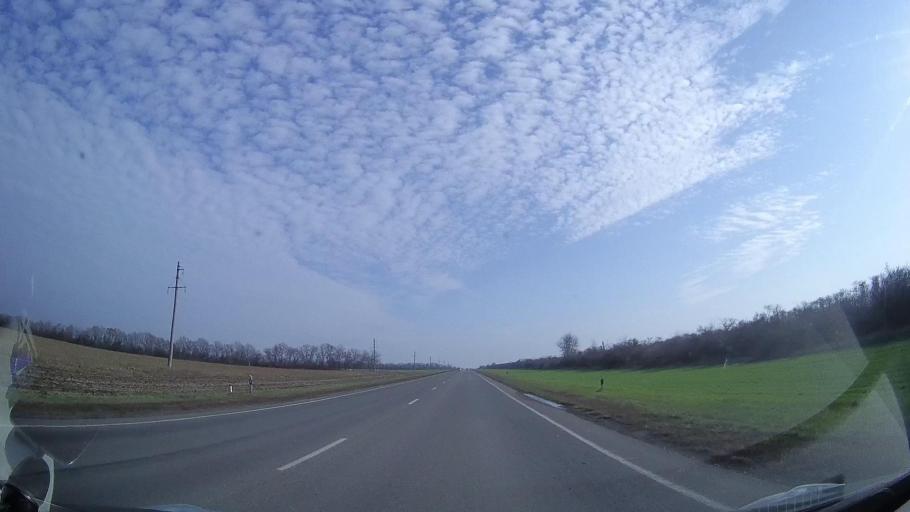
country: RU
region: Rostov
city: Gigant
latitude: 46.5255
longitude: 41.2392
